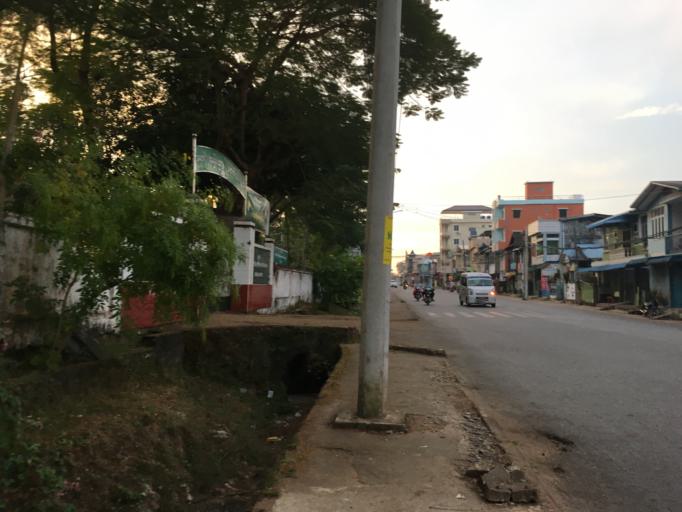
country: MM
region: Mon
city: Mawlamyine
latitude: 16.4710
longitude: 97.6255
